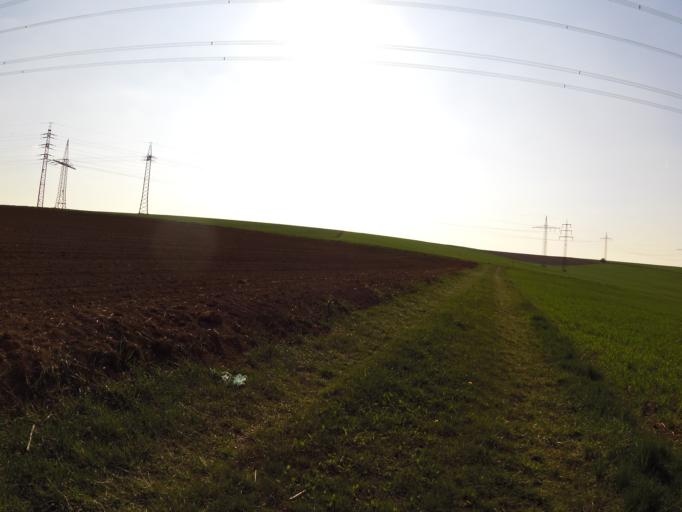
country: DE
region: Bavaria
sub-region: Regierungsbezirk Unterfranken
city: Theilheim
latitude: 49.7662
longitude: 10.0528
